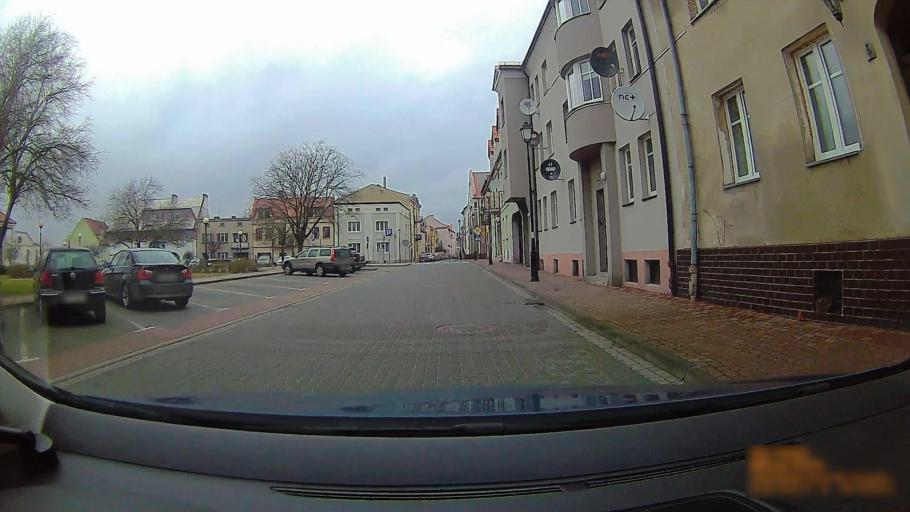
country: PL
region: Greater Poland Voivodeship
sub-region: Konin
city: Konin
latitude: 52.2105
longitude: 18.2536
